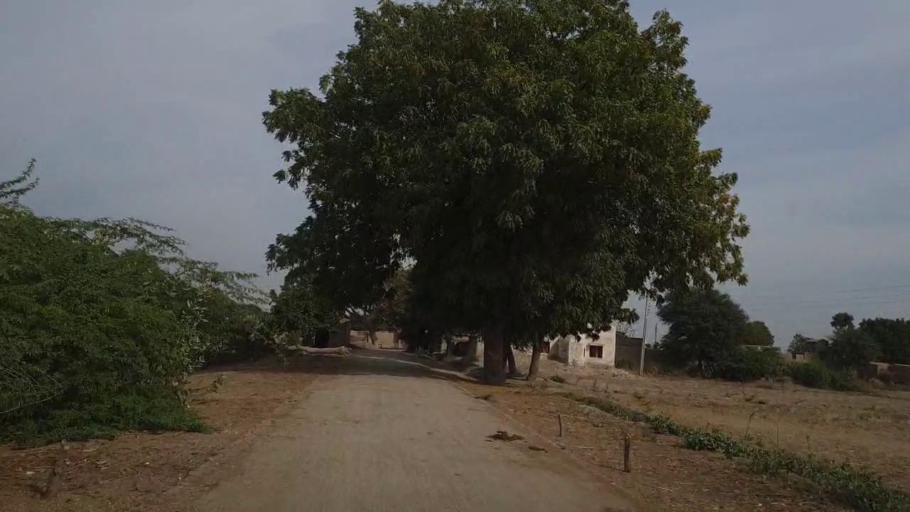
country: PK
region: Sindh
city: Nabisar
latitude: 25.0307
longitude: 69.5626
